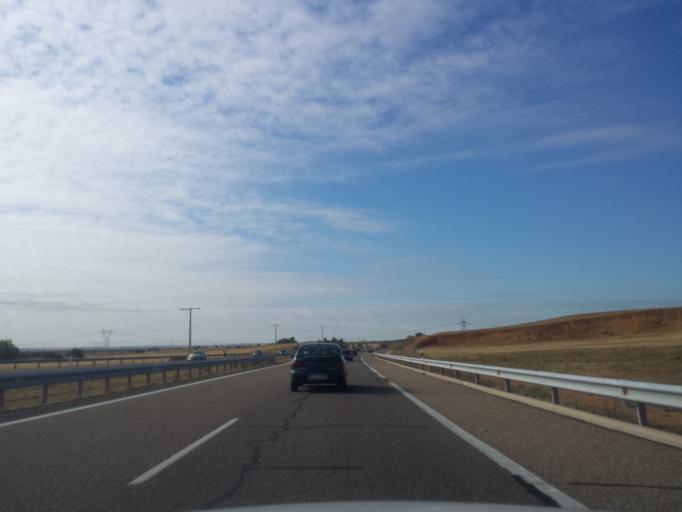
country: ES
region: Castille and Leon
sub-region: Provincia de Leon
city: Ardon
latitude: 42.4584
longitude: -5.5814
